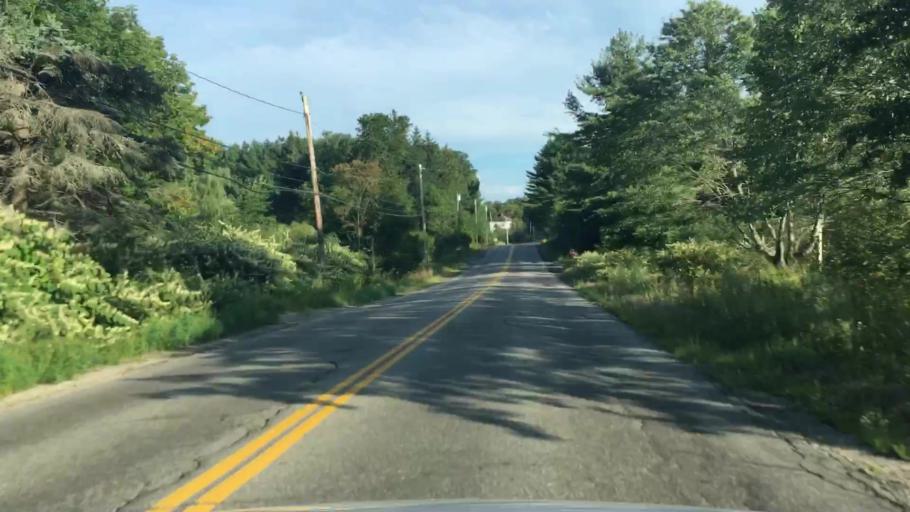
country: US
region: Maine
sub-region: Cumberland County
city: Westbrook
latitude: 43.7091
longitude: -70.3830
